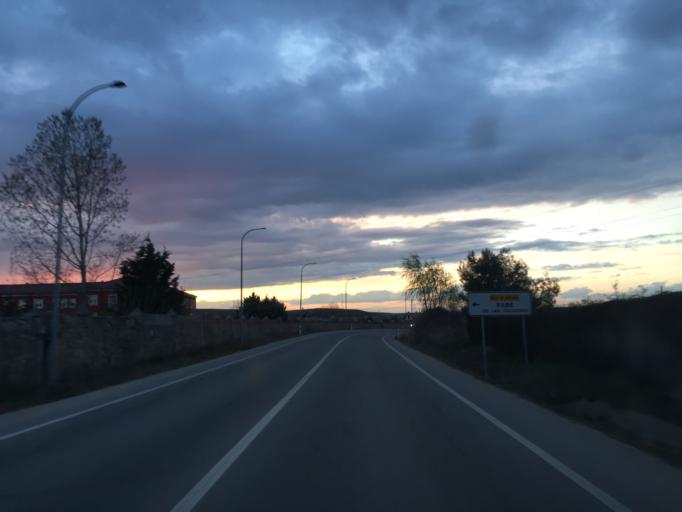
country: ES
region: Castille and Leon
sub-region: Provincia de Burgos
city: Tardajos
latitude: 42.3506
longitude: -3.8172
